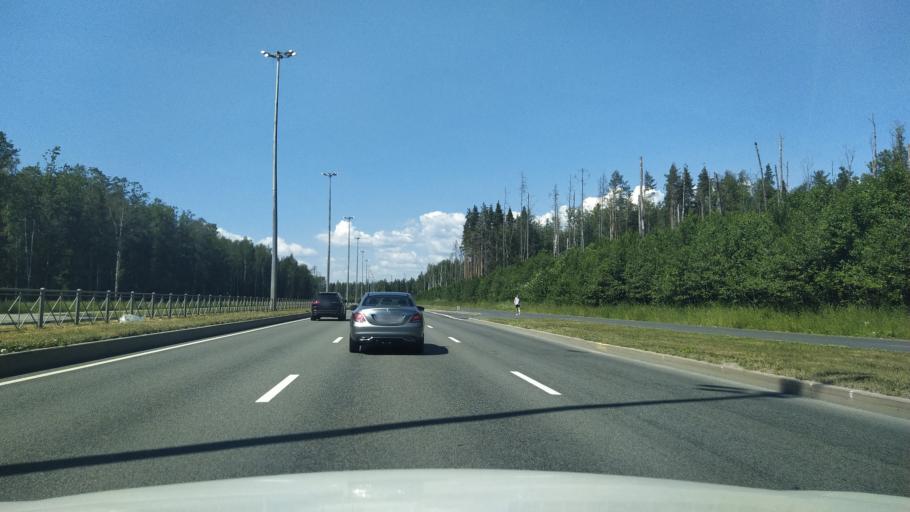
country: RU
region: Leningrad
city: Untolovo
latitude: 60.0581
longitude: 30.2209
